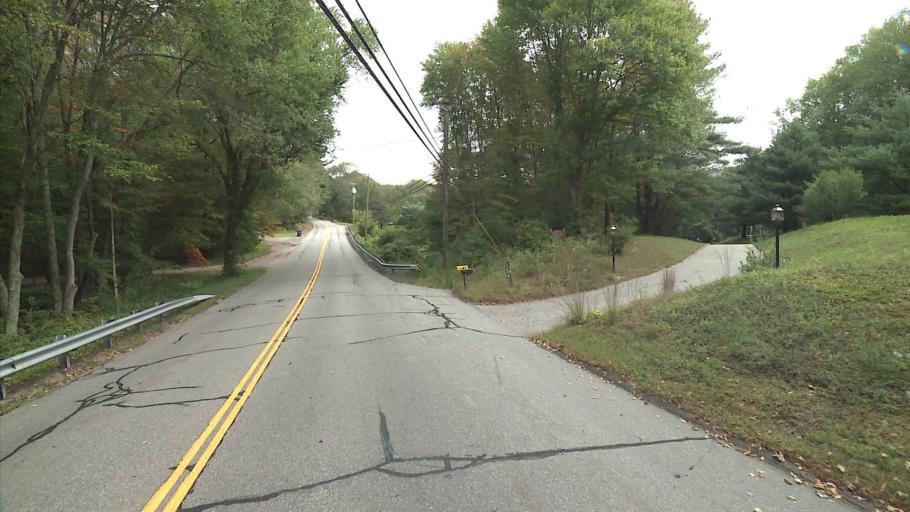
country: US
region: Connecticut
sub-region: Tolland County
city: South Coventry
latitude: 41.7788
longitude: -72.2844
